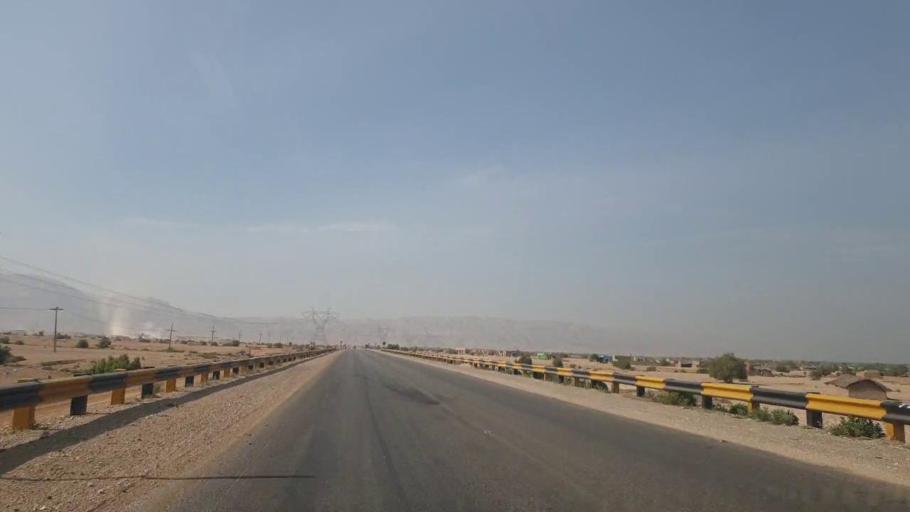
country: PK
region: Sindh
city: Sehwan
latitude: 26.2063
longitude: 67.9298
